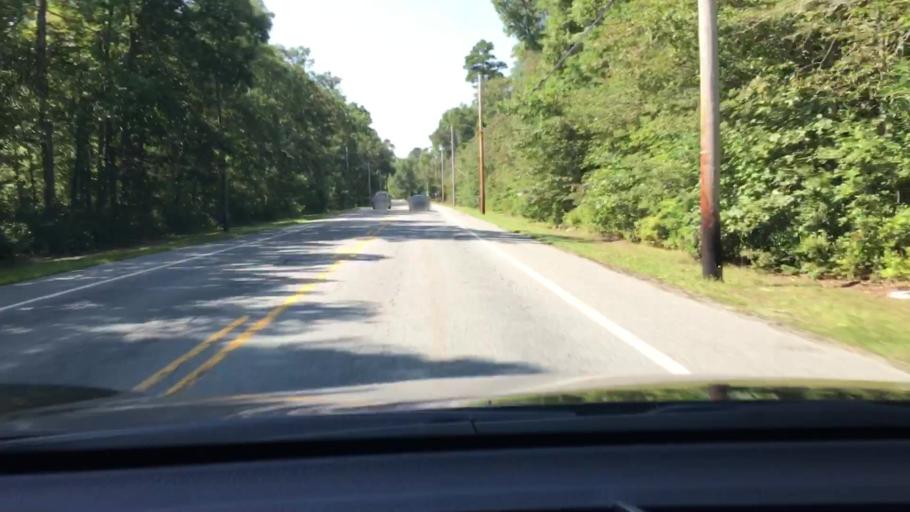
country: US
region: New Jersey
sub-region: Cape May County
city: Woodbine
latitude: 39.2878
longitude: -74.7891
